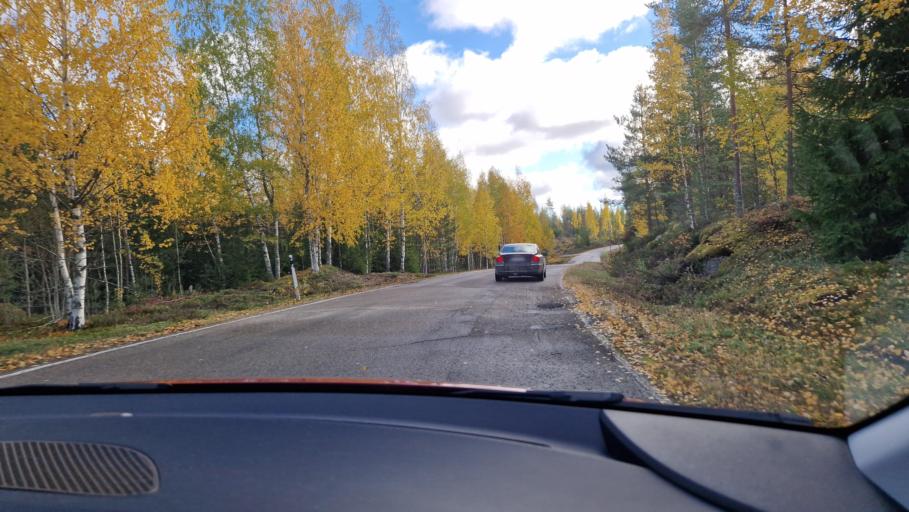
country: FI
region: South Karelia
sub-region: Lappeenranta
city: Lemi
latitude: 60.9933
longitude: 27.7148
